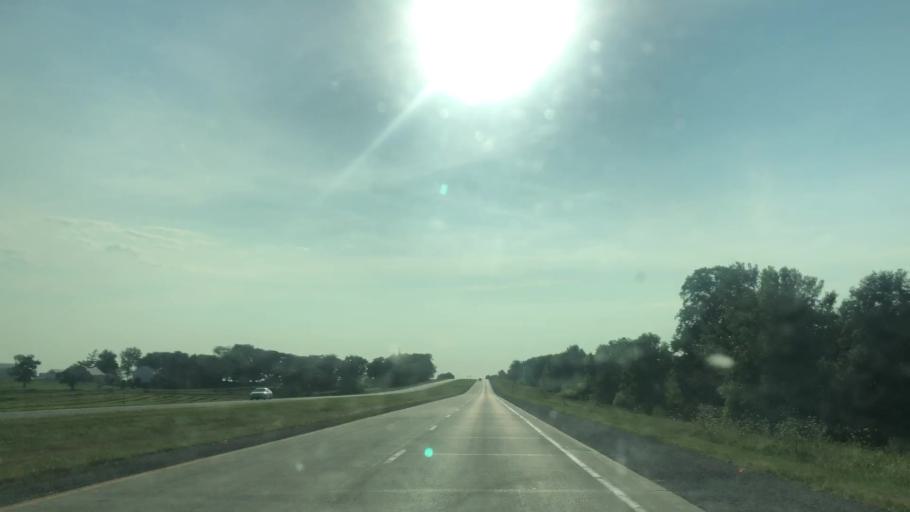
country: US
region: Iowa
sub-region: Story County
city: Nevada
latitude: 42.0077
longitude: -93.3819
